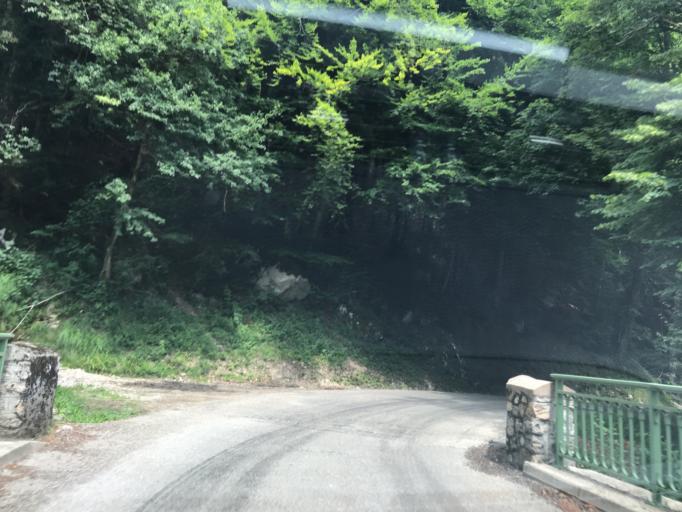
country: FR
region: Rhone-Alpes
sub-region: Departement de l'Isere
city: Barraux
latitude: 45.4553
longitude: 5.9554
